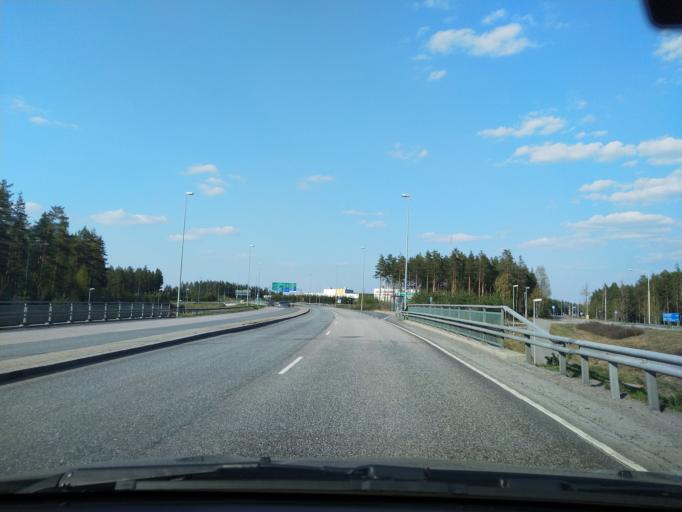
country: FI
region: Uusimaa
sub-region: Helsinki
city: Lohja
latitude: 60.2695
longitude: 24.1165
